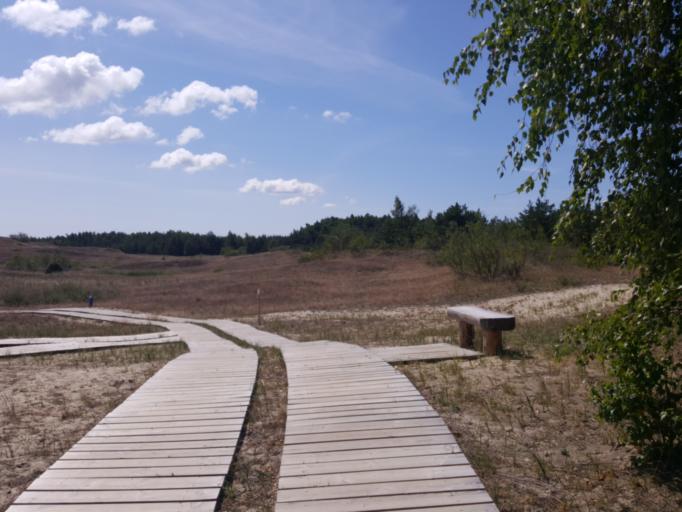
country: LT
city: Neringa
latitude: 55.4408
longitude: 21.0760
